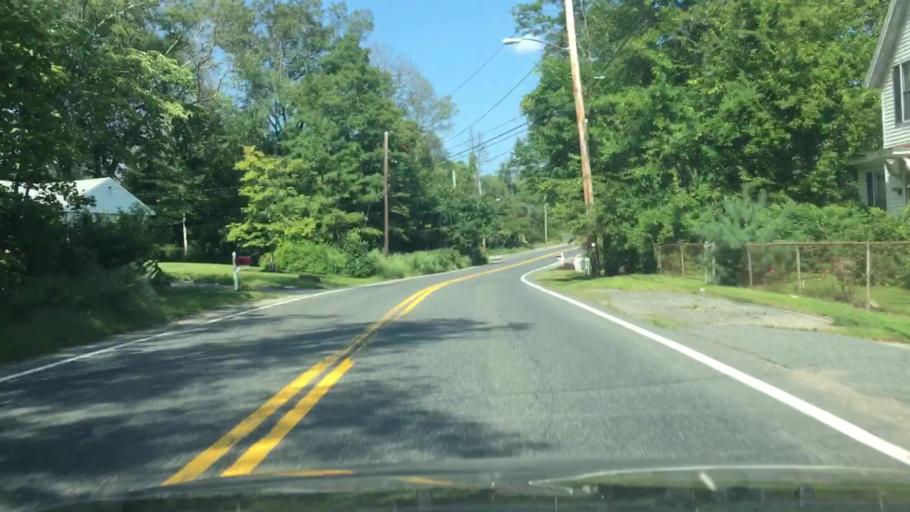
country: US
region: Massachusetts
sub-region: Worcester County
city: Milford
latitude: 42.1677
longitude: -71.4786
